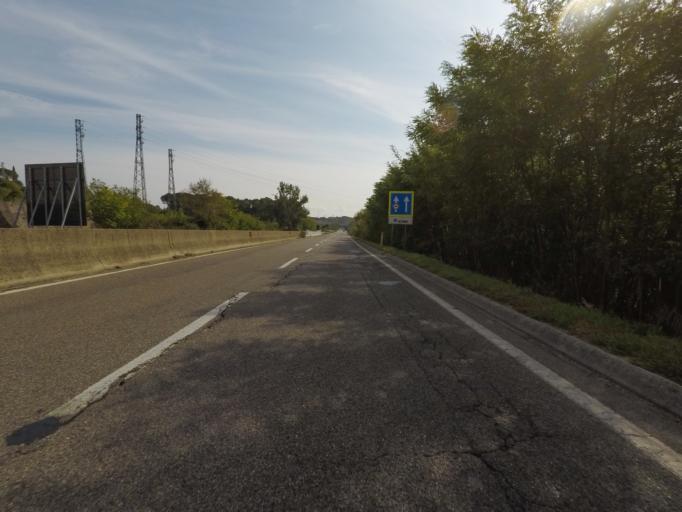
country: IT
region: Tuscany
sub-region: Provincia di Siena
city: Siena
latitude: 43.2983
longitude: 11.3289
